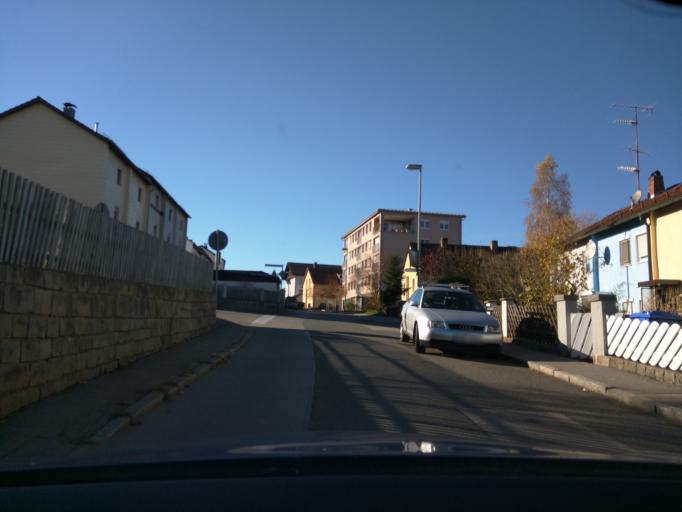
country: DE
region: Bavaria
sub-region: Lower Bavaria
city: Salzweg
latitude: 48.5850
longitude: 13.4960
